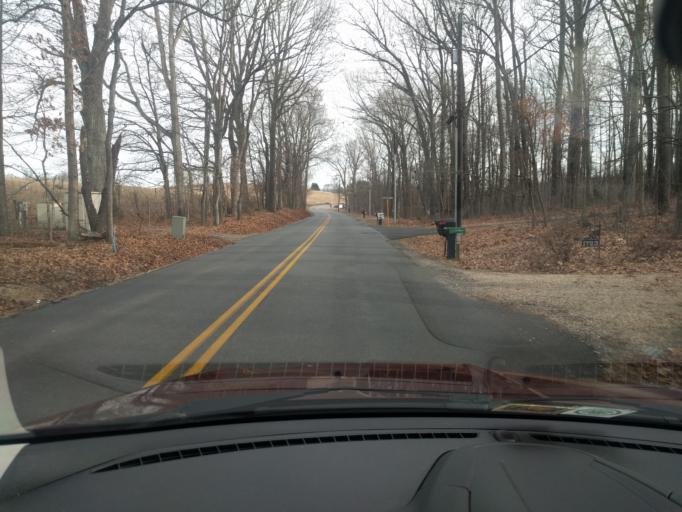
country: US
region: Virginia
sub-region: Augusta County
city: Fishersville
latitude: 38.0842
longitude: -78.9546
